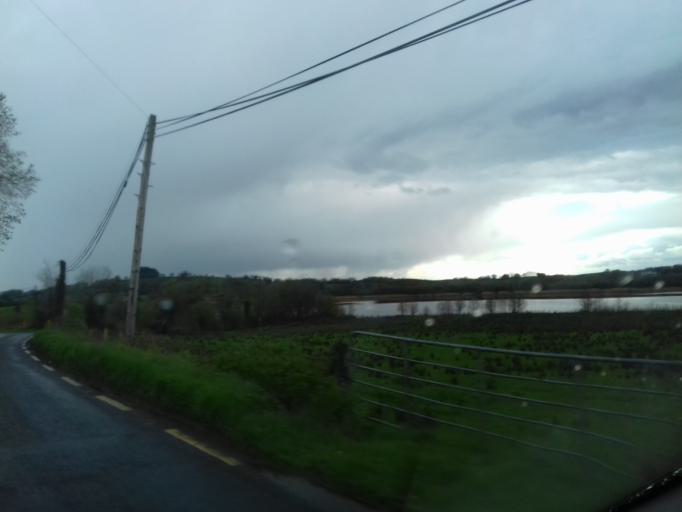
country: IE
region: Ulster
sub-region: An Cabhan
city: Ballyconnell
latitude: 54.1319
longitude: -7.6894
